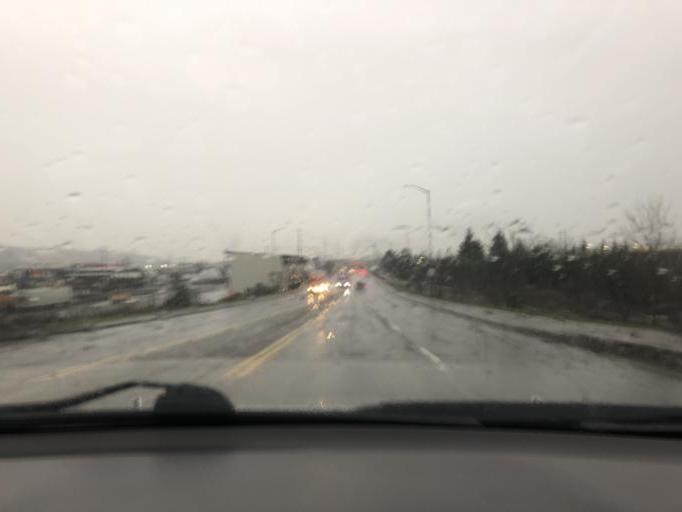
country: US
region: Washington
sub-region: Pierce County
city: Tacoma
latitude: 47.2452
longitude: -122.4128
